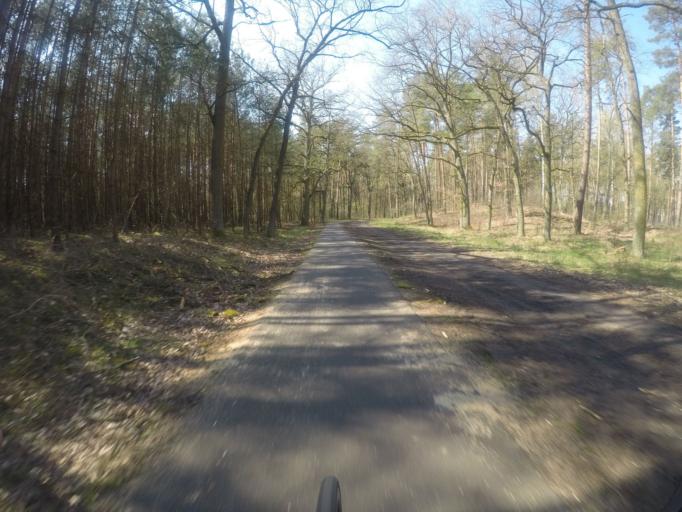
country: DE
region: Brandenburg
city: Nauen
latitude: 52.6594
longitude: 12.9411
